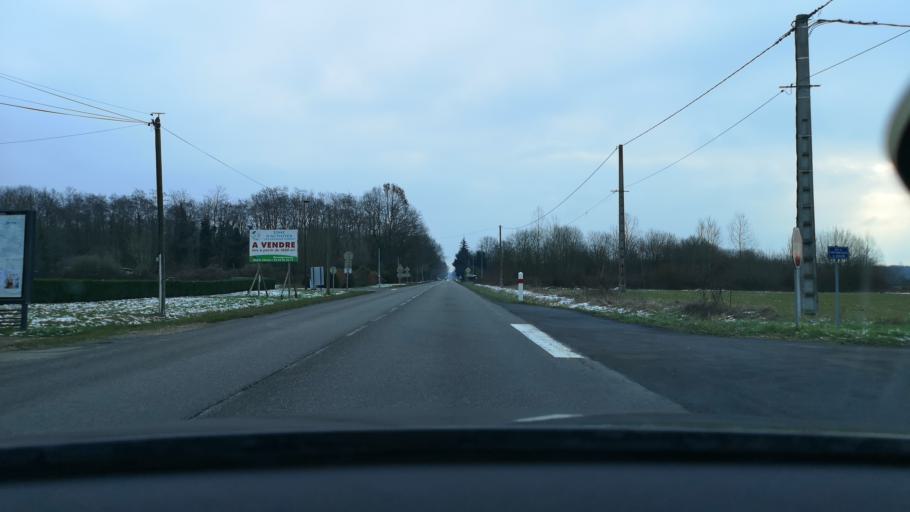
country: FR
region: Bourgogne
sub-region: Departement de Saone-et-Loire
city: Saint-Marcel
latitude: 46.7831
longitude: 4.9335
